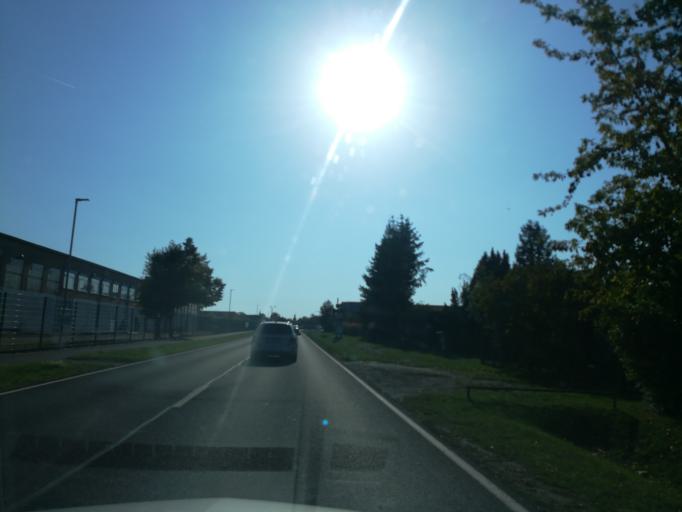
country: DE
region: Saxony-Anhalt
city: Gommern
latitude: 52.0797
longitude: 11.8182
